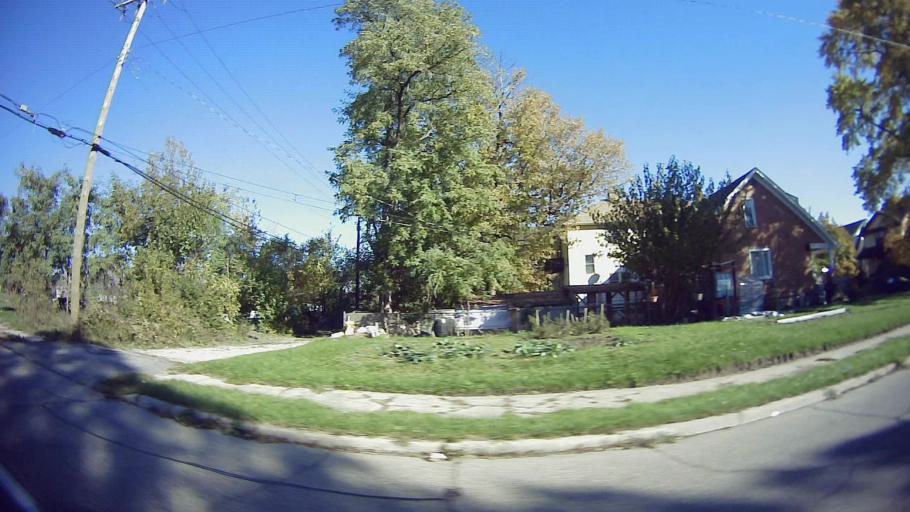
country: US
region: Michigan
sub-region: Wayne County
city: Highland Park
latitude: 42.3885
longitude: -83.1107
